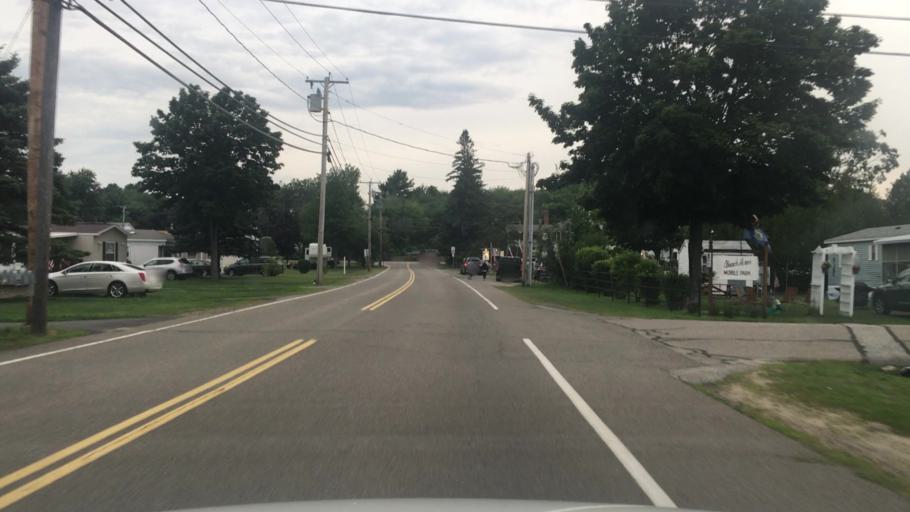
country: US
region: Maine
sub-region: York County
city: Wells Beach Station
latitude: 43.2911
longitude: -70.5881
